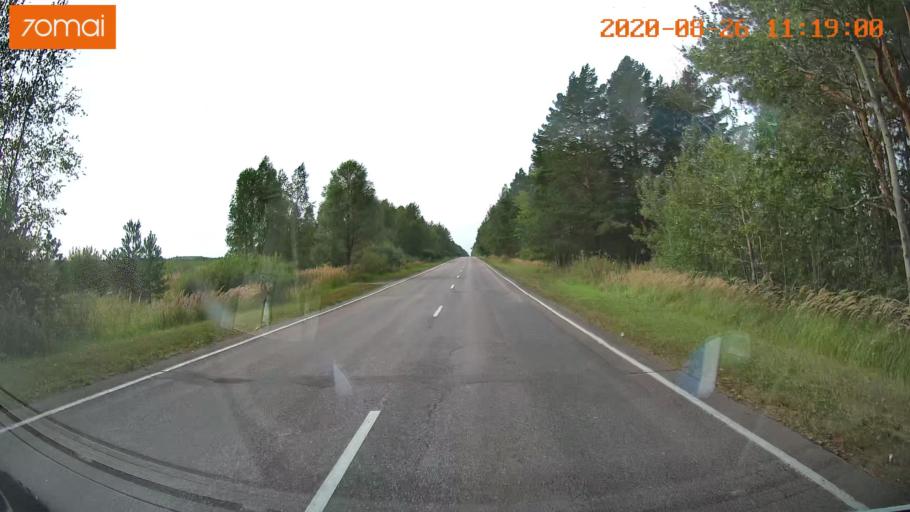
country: RU
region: Rjazan
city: Shilovo
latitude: 54.4041
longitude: 41.0874
